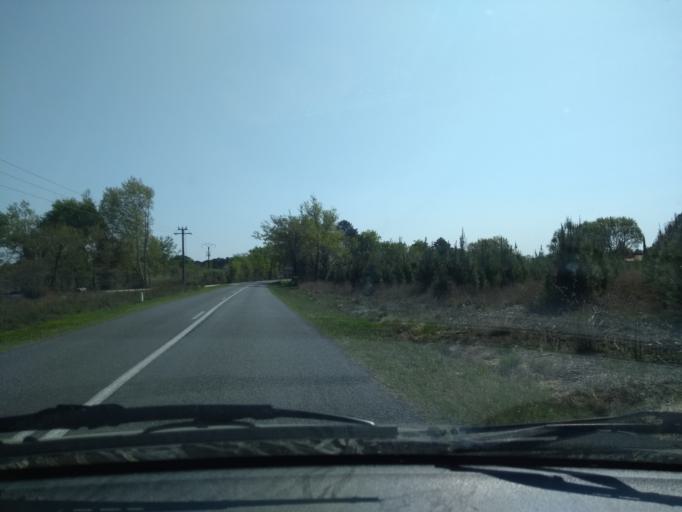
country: FR
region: Aquitaine
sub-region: Departement de la Gironde
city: Belin-Beliet
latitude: 44.5284
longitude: -0.6717
